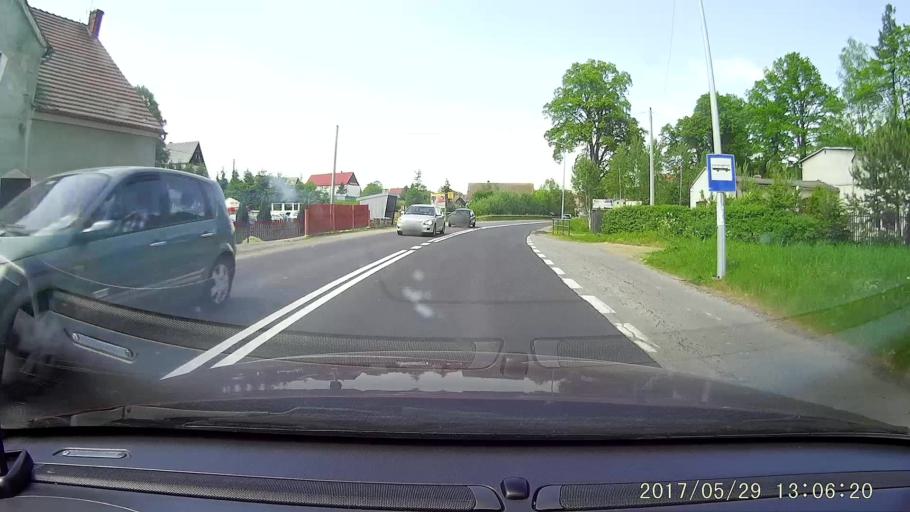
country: PL
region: Lower Silesian Voivodeship
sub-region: Powiat jeleniogorski
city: Stara Kamienica
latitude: 50.9505
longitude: 15.5820
